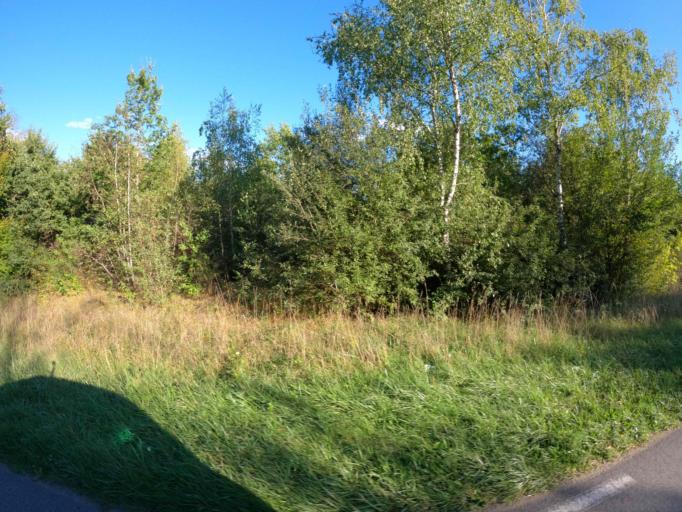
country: FR
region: Bourgogne
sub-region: Departement de Saone-et-Loire
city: Saint-Eusebe
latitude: 46.7347
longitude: 4.4421
